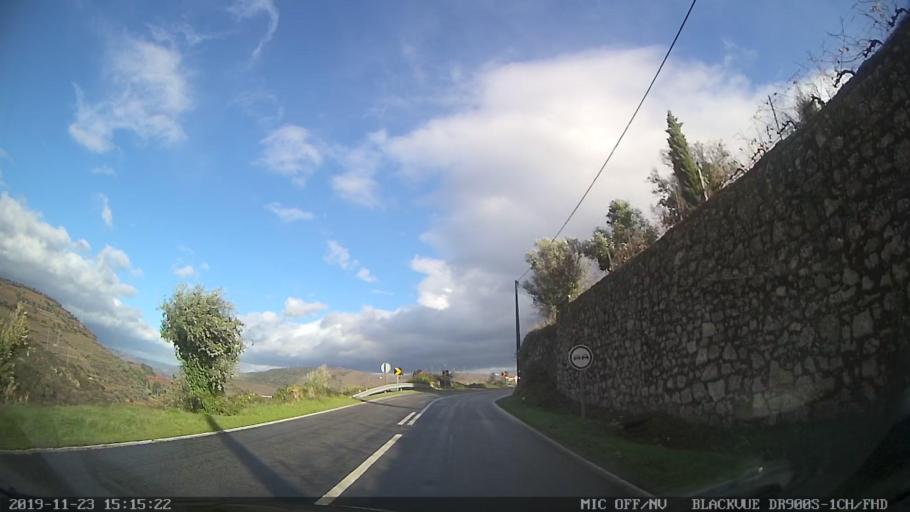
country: PT
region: Vila Real
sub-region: Peso da Regua
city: Peso da Regua
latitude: 41.1290
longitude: -7.7905
